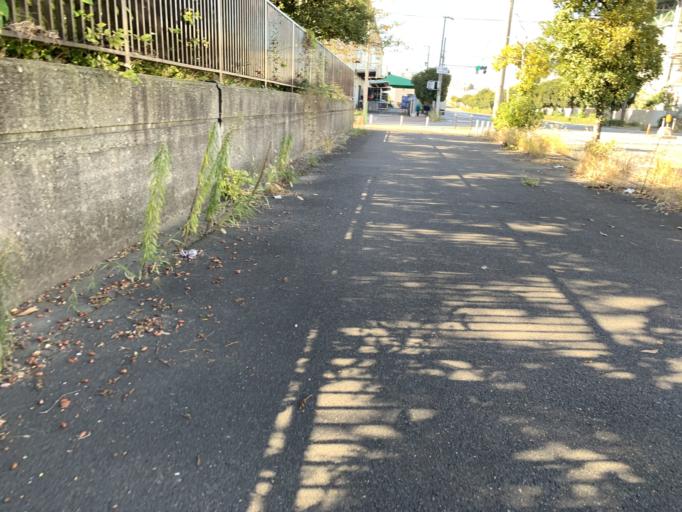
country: JP
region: Hyogo
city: Amagasaki
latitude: 34.6502
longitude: 135.4421
